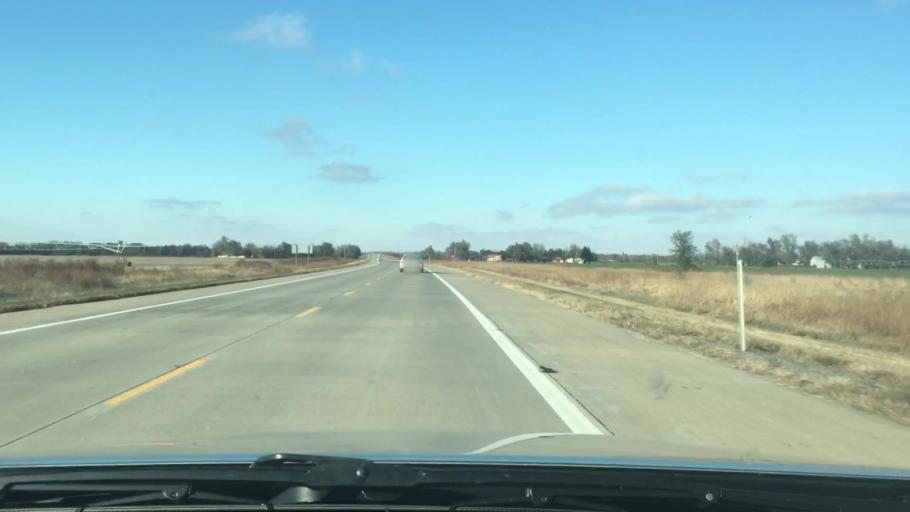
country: US
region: Kansas
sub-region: Reno County
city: Hutchinson
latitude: 38.0659
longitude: -97.9862
